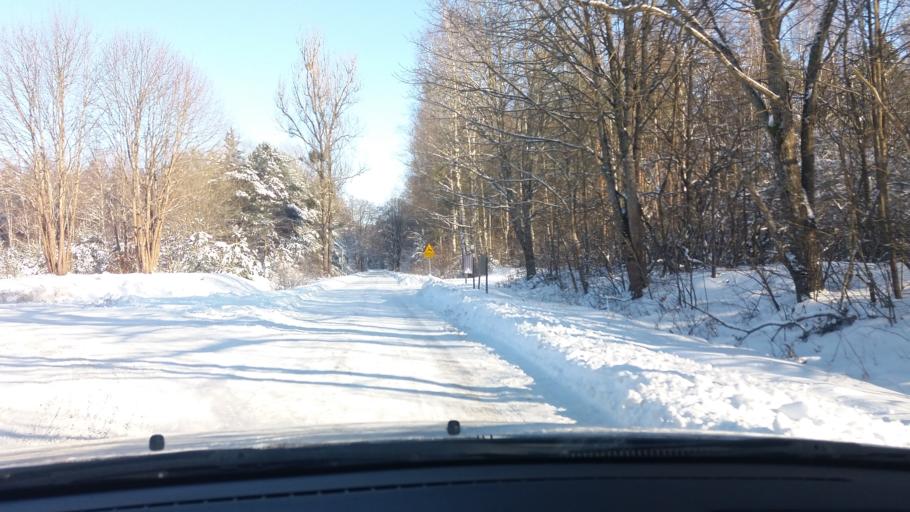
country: PL
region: Warmian-Masurian Voivodeship
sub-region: Powiat nidzicki
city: Nidzica
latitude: 53.3518
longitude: 20.6170
